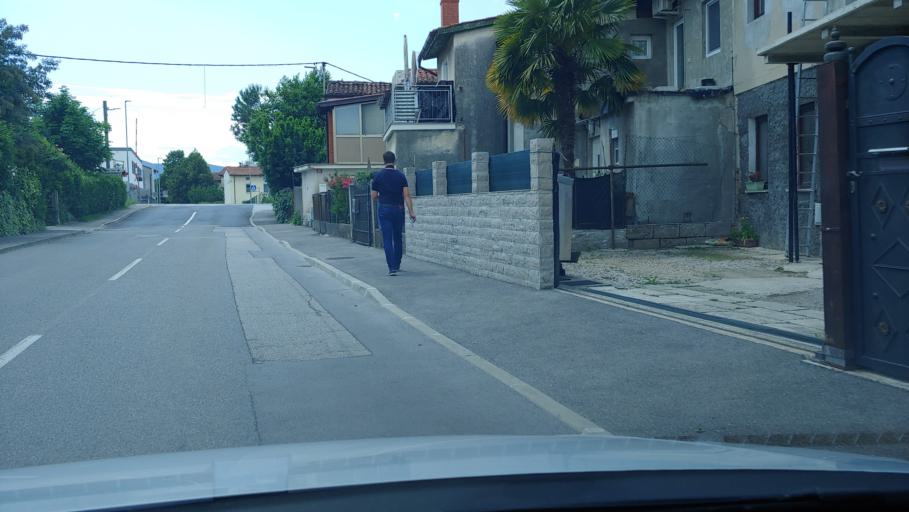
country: SI
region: Sempeter-Vrtojba
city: Sempeter pri Gorici
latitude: 45.9266
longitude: 13.6406
